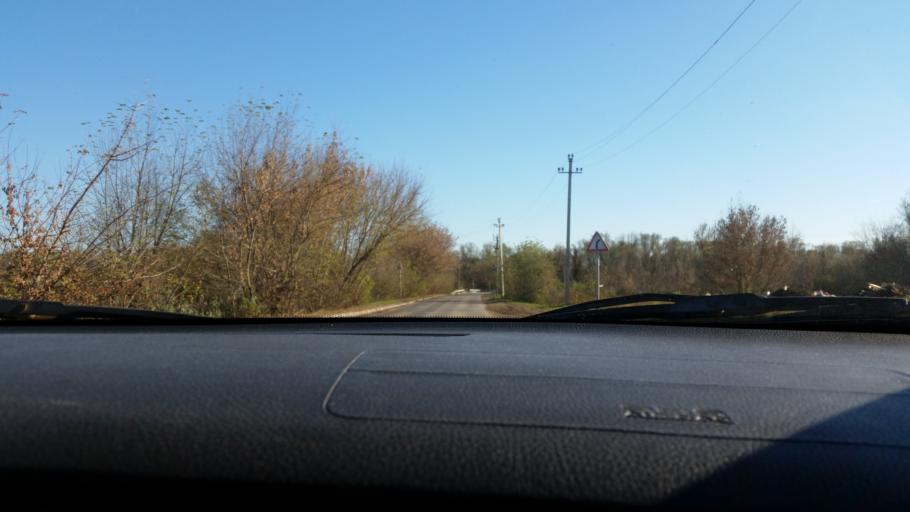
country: RU
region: Lipetsk
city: Gryazi
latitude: 52.4724
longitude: 39.9596
